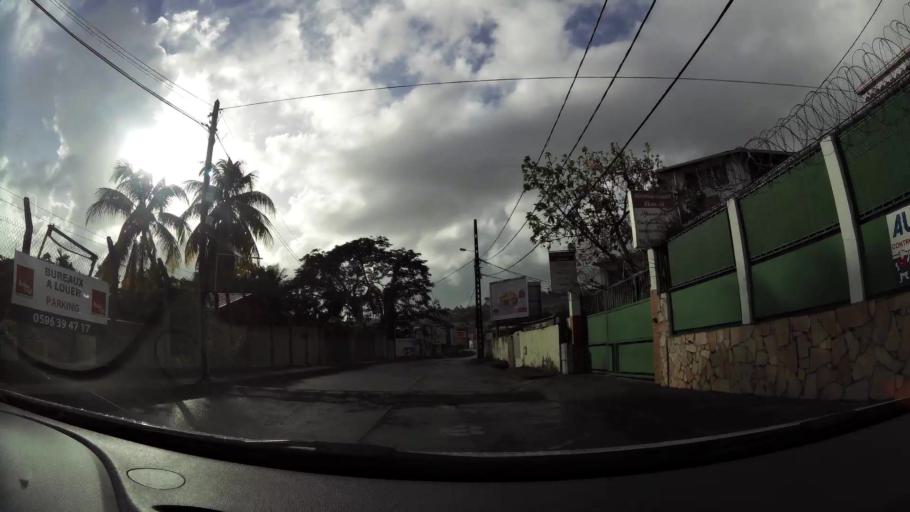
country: MQ
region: Martinique
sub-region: Martinique
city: Fort-de-France
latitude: 14.6168
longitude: -61.0472
